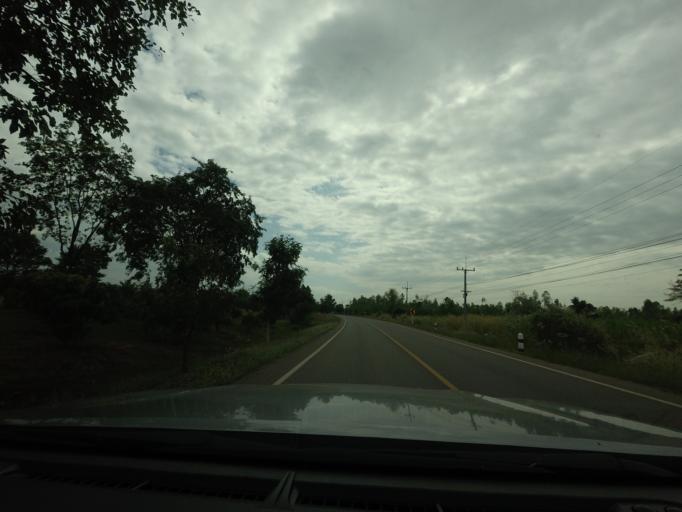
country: TH
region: Phitsanulok
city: Noen Maprang
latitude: 16.6088
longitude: 100.6201
